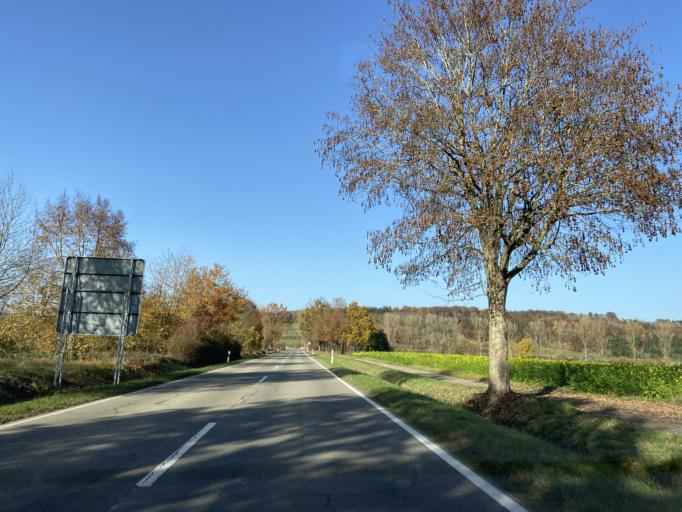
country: DE
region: Baden-Wuerttemberg
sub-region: Tuebingen Region
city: Ennetach
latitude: 48.0321
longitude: 9.2900
